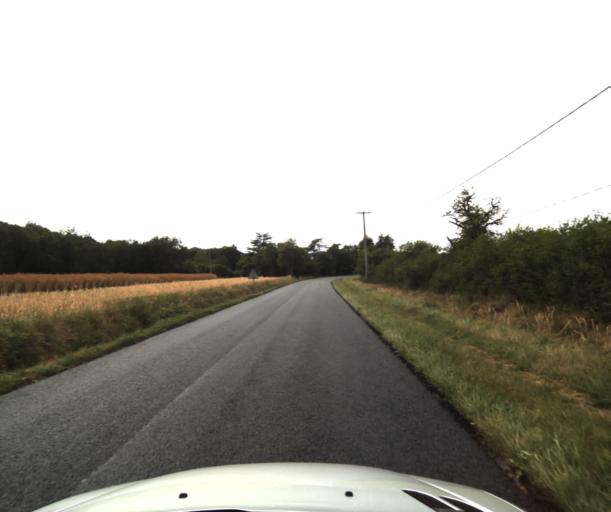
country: FR
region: Midi-Pyrenees
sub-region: Departement de la Haute-Garonne
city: Labastidette
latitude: 43.4860
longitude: 1.2151
